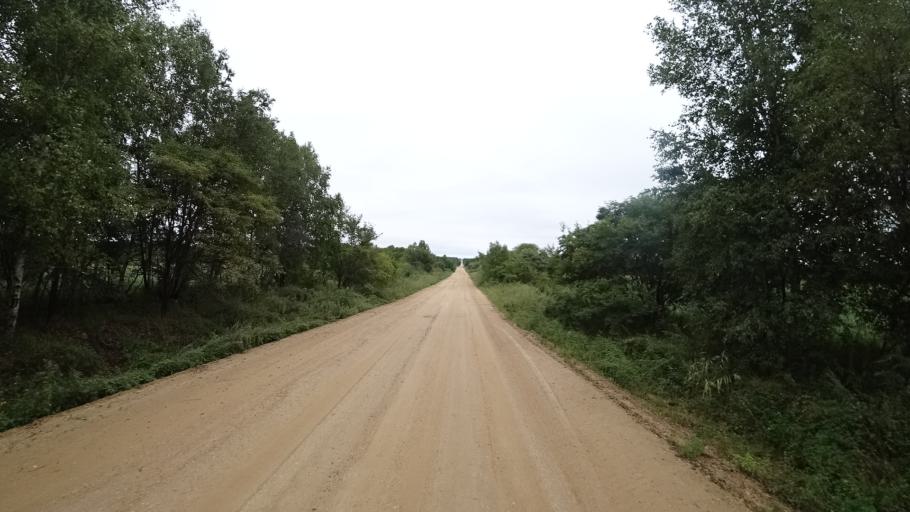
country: RU
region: Primorskiy
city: Ivanovka
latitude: 44.0636
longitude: 132.5704
